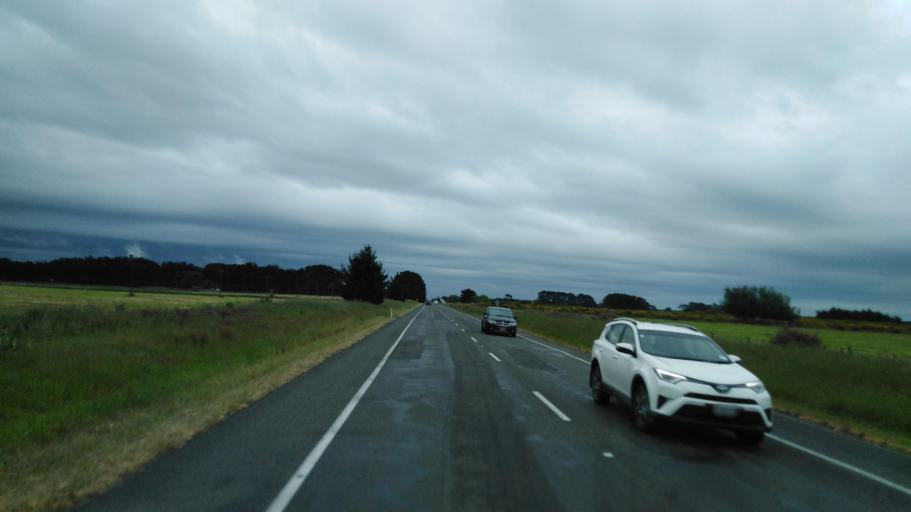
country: NZ
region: Manawatu-Wanganui
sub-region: Horowhenua District
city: Foxton
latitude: -40.4245
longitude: 175.3037
